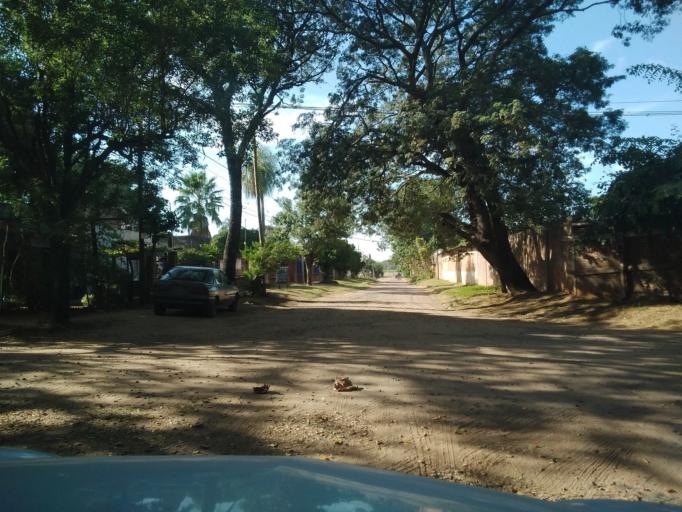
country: AR
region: Corrientes
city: Corrientes
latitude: -27.5043
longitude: -58.8108
